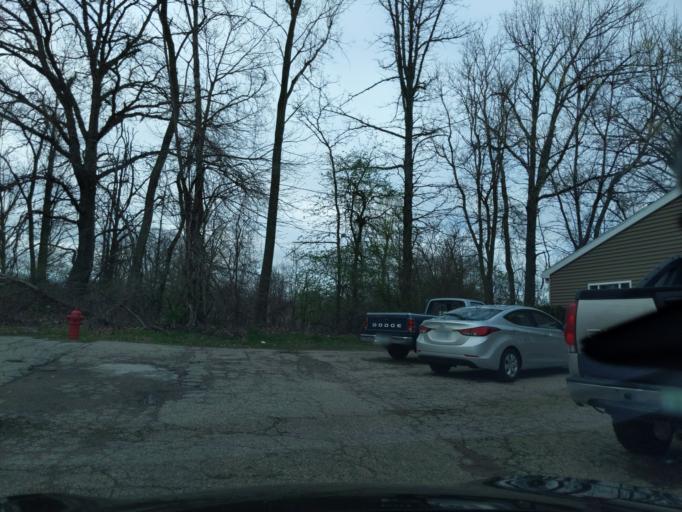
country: US
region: Michigan
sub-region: Ingham County
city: Edgemont Park
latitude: 42.7301
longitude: -84.5919
